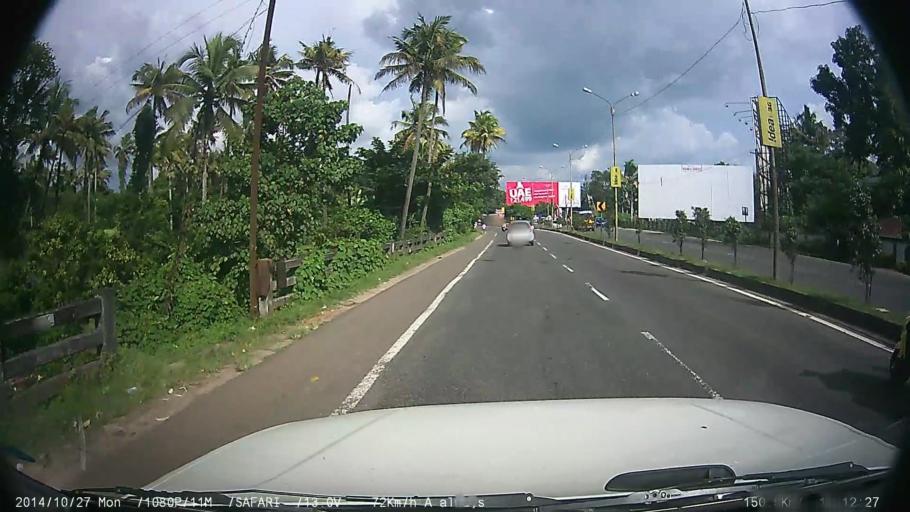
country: IN
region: Kerala
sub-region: Ernakulam
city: Aluva
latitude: 10.1303
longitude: 76.3500
